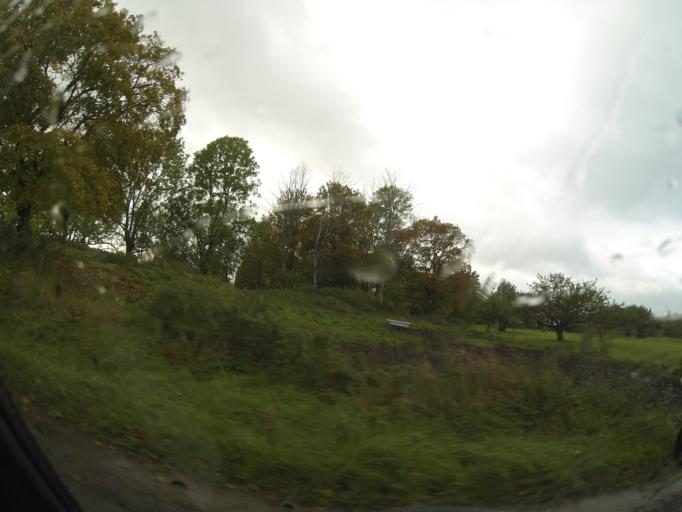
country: SE
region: Soedermanland
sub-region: Eskilstuna Kommun
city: Kvicksund
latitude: 59.3392
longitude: 16.2992
